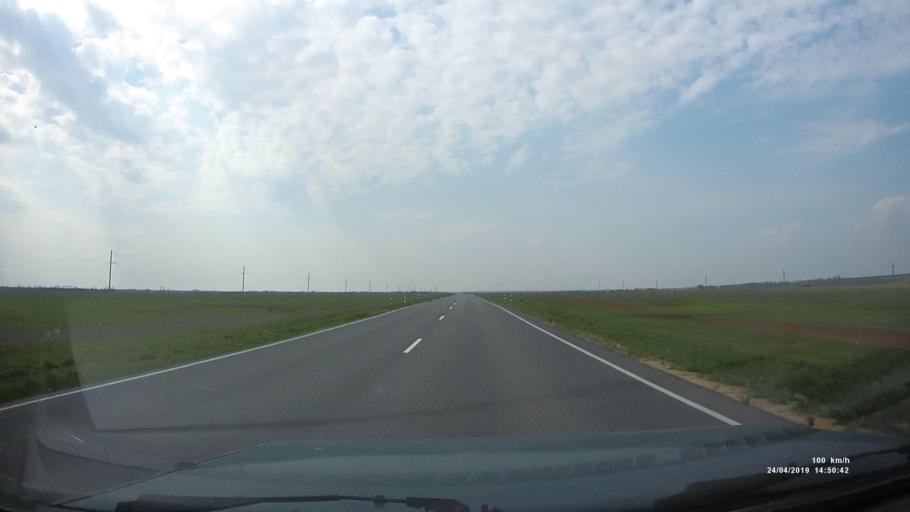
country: RU
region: Rostov
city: Remontnoye
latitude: 46.5193
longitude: 43.7147
